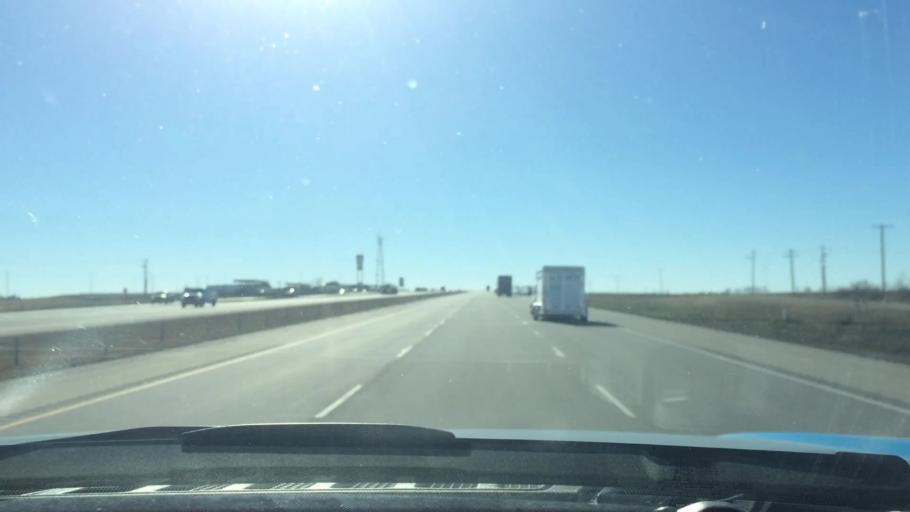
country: CA
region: Alberta
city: Crossfield
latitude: 51.4184
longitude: -114.0021
